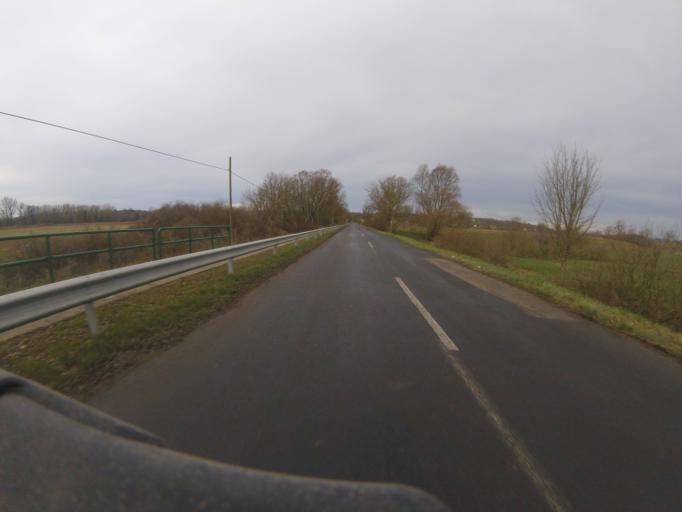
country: HU
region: Tolna
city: Dombovar
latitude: 46.3602
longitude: 18.1215
